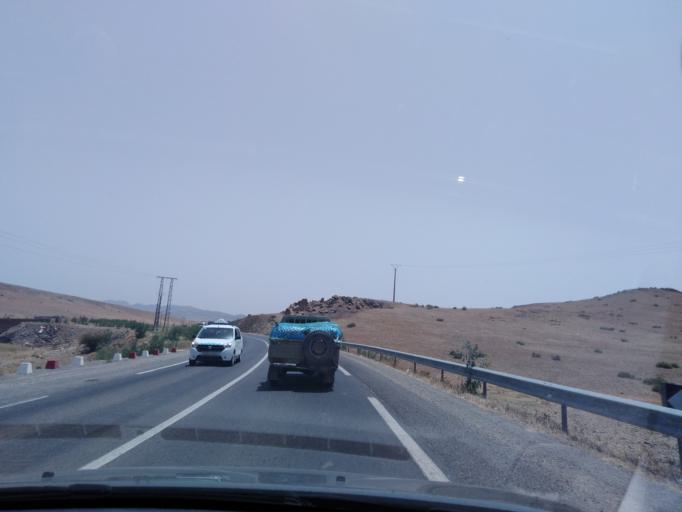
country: MA
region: Marrakech-Tensift-Al Haouz
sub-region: Kelaa-Des-Sraghna
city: Sidi Bou Othmane
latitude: 31.9285
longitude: -8.2024
